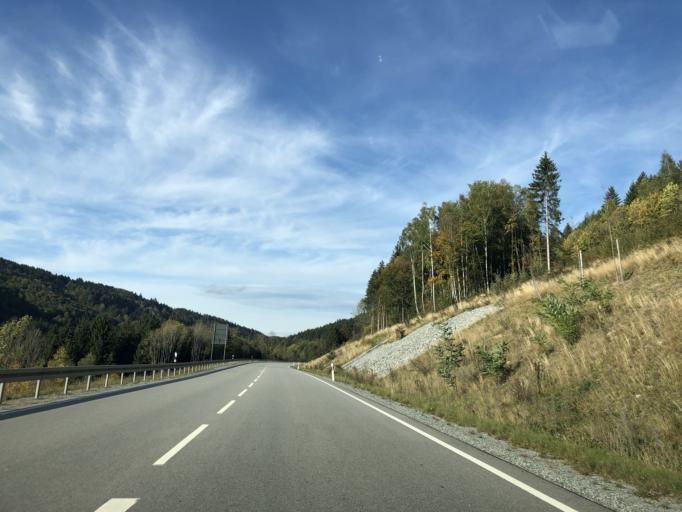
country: DE
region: Bavaria
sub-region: Lower Bavaria
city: Grafling
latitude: 48.9243
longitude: 12.9793
